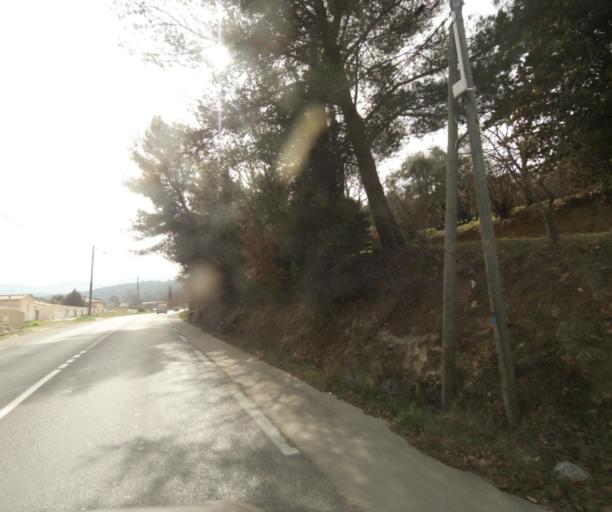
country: FR
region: Provence-Alpes-Cote d'Azur
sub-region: Departement des Bouches-du-Rhone
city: Gardanne
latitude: 43.4429
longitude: 5.4579
